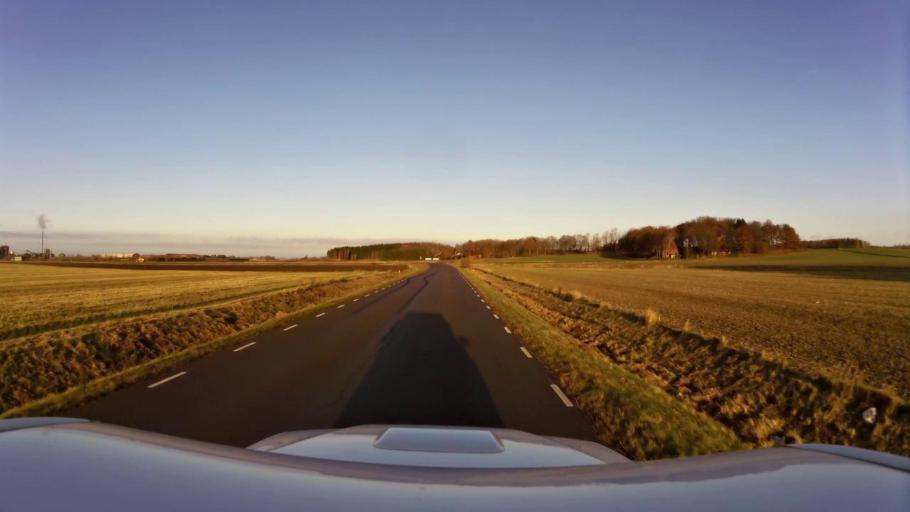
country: SE
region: OEstergoetland
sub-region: Linkopings Kommun
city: Ekangen
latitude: 58.4389
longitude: 15.6765
